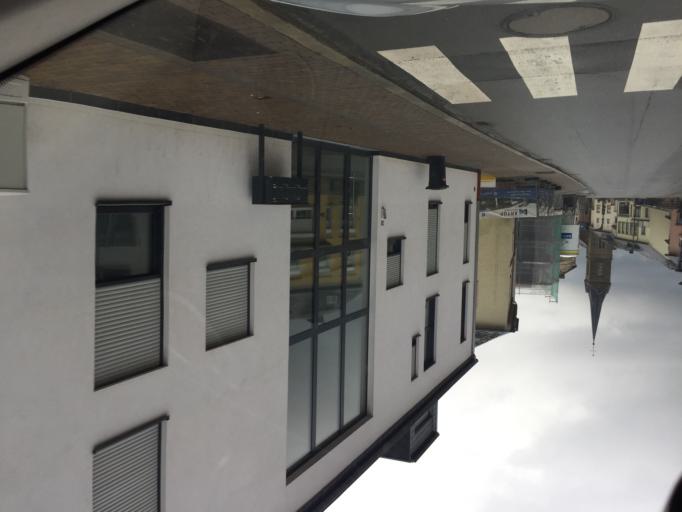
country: LU
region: Diekirch
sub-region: Canton de Diekirch
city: Diekirch
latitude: 49.8654
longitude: 6.1798
